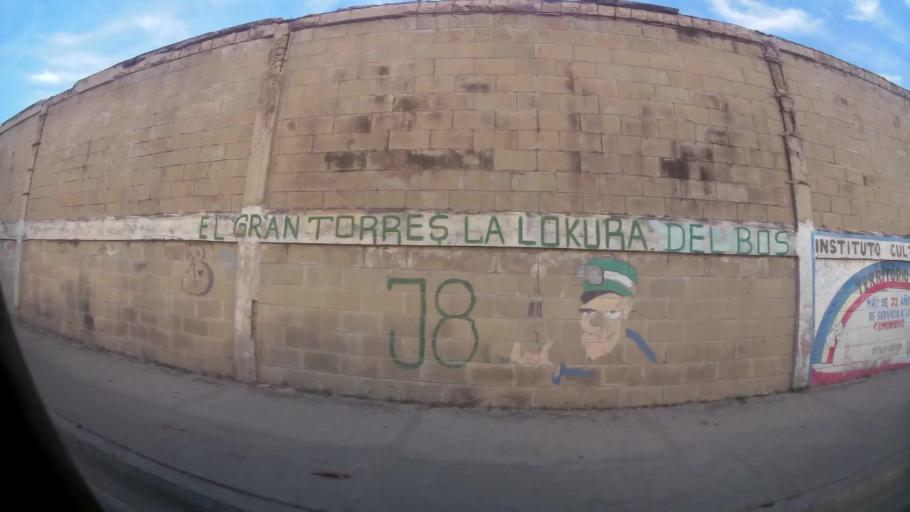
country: CO
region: Atlantico
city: Barranquilla
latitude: 10.9531
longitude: -74.8237
